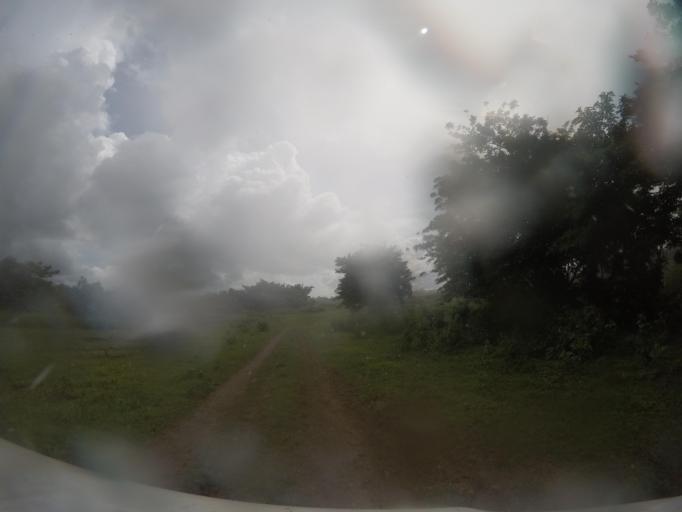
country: TL
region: Lautem
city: Lospalos
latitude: -8.5075
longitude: 127.0096
